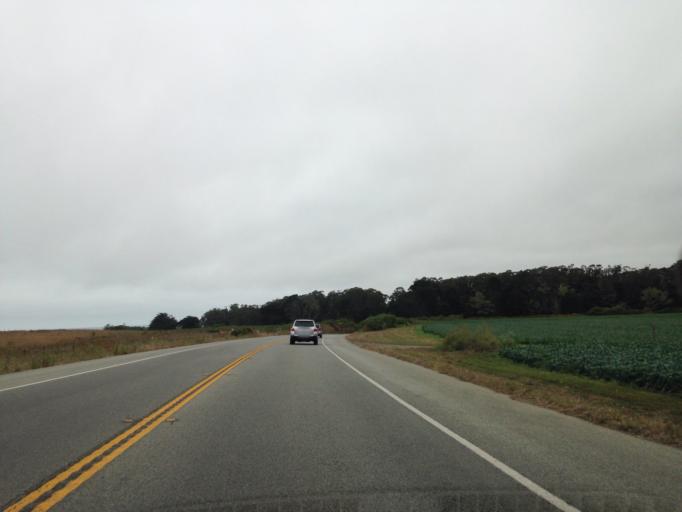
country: US
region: California
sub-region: San Mateo County
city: Half Moon Bay
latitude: 37.3994
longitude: -122.4182
